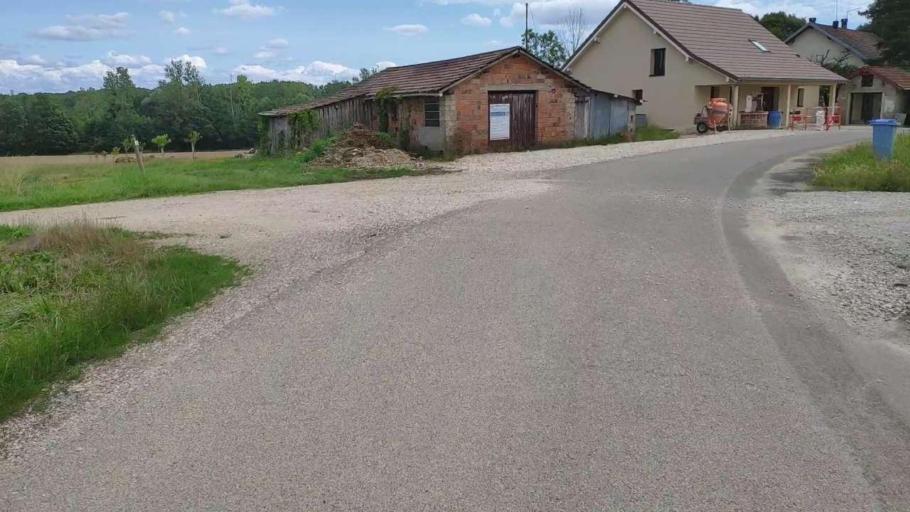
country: FR
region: Franche-Comte
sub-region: Departement du Jura
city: Chaussin
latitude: 46.8808
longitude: 5.4438
